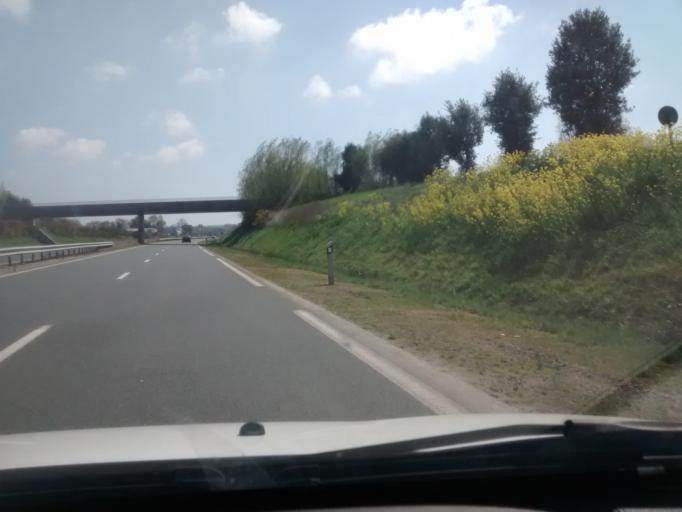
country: FR
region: Brittany
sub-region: Departement des Cotes-d'Armor
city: Begard
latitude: 48.6450
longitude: -3.3273
